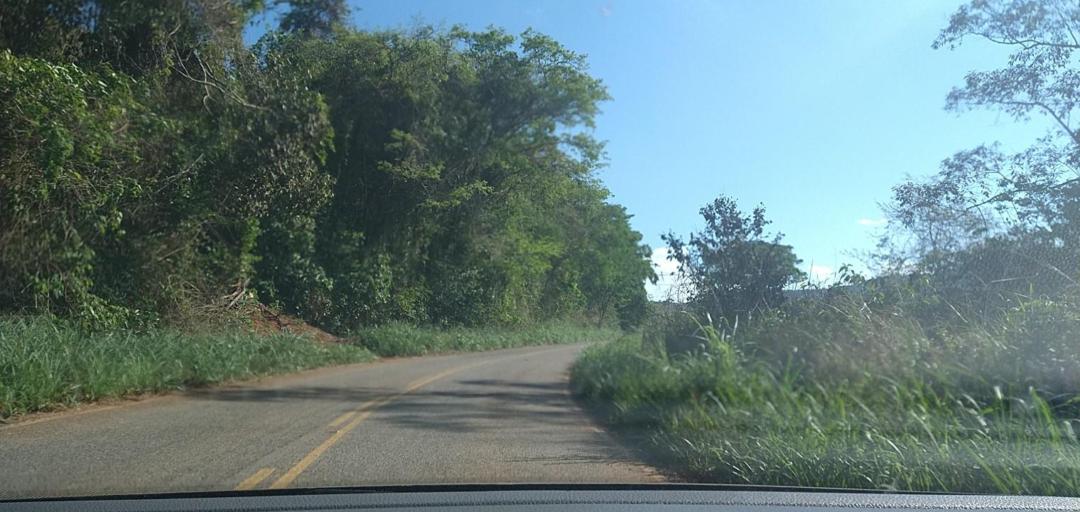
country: BR
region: Minas Gerais
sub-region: Alvinopolis
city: Alvinopolis
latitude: -20.1805
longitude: -42.9314
